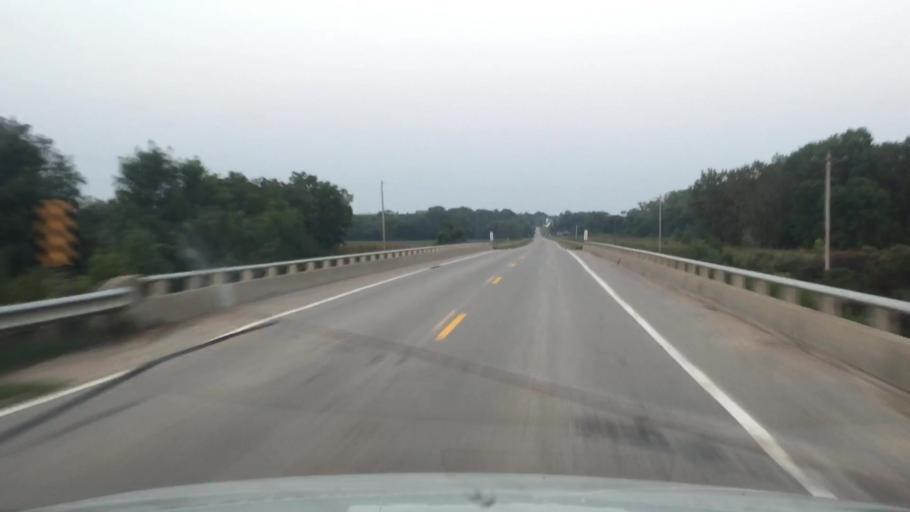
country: US
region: Iowa
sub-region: Warren County
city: Indianola
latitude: 41.1871
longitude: -93.6135
